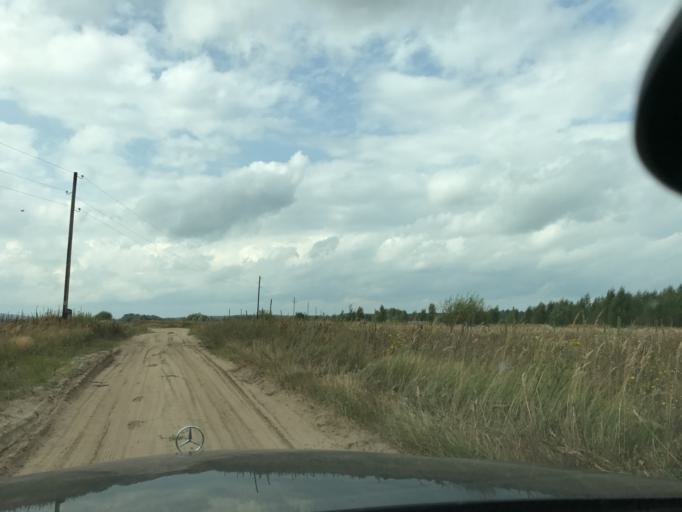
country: RU
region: Nizjnij Novgorod
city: Vacha
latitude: 55.9807
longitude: 42.7833
